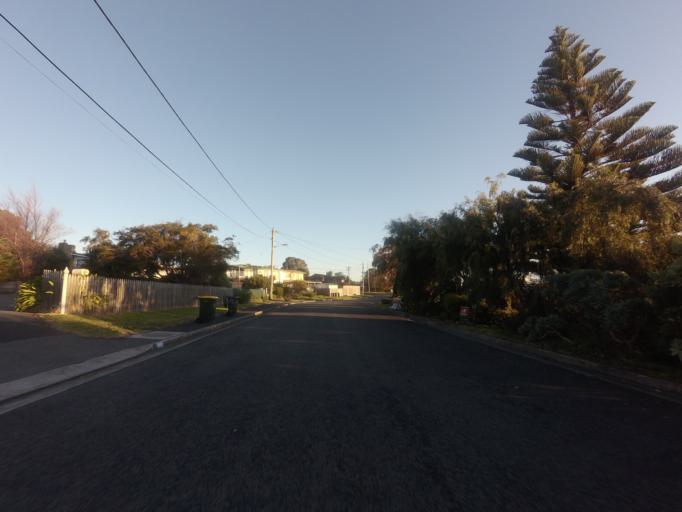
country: AU
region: Tasmania
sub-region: Sorell
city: Sorell
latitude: -42.8012
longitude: 147.5271
